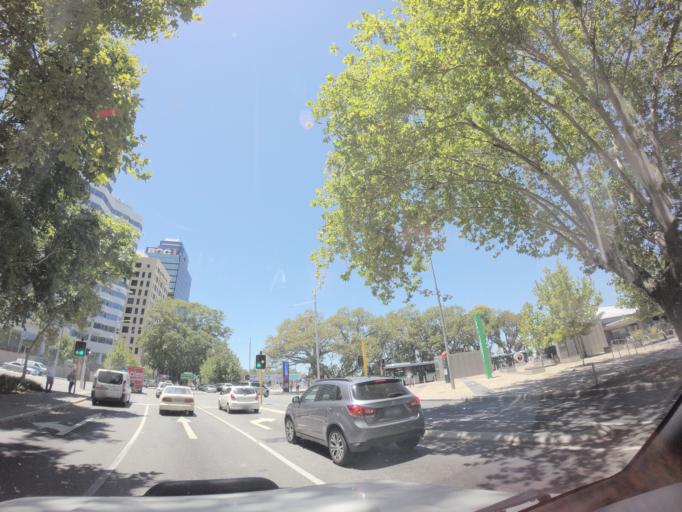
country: AU
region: Western Australia
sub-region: Cambridge
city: Perth
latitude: -31.9559
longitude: 115.8555
